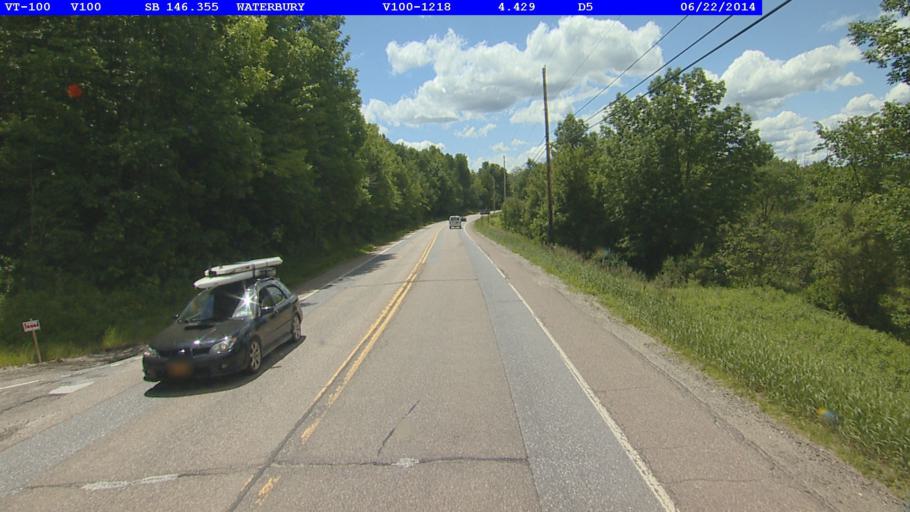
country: US
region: Vermont
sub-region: Washington County
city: Waterbury
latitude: 44.3928
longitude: -72.7190
